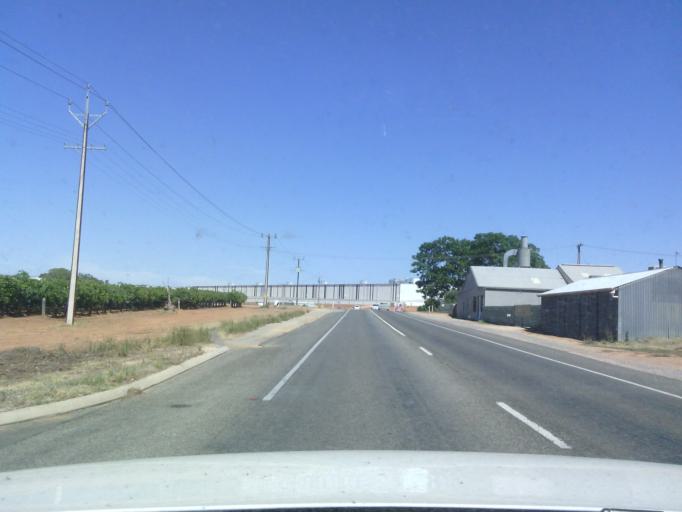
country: AU
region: South Australia
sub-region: Berri and Barmera
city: Monash
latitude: -34.2762
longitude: 140.5358
